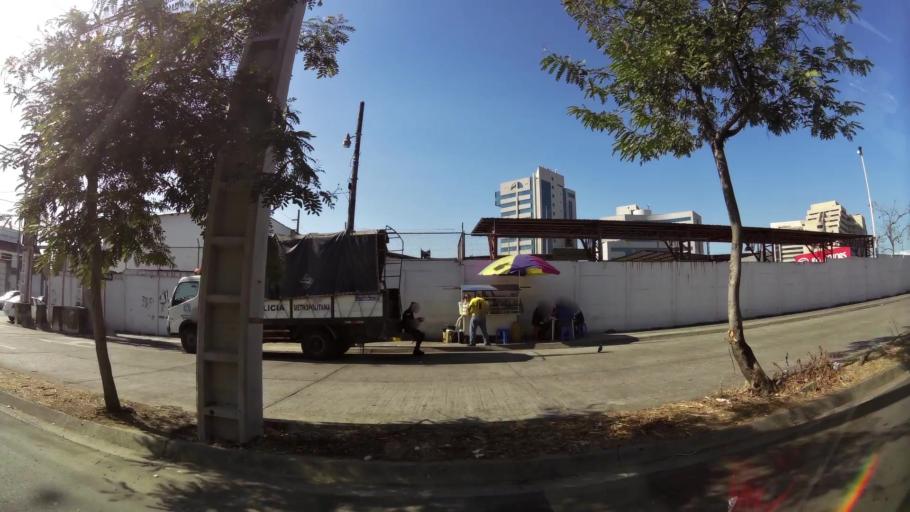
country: EC
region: Guayas
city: Eloy Alfaro
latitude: -2.1565
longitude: -79.8978
